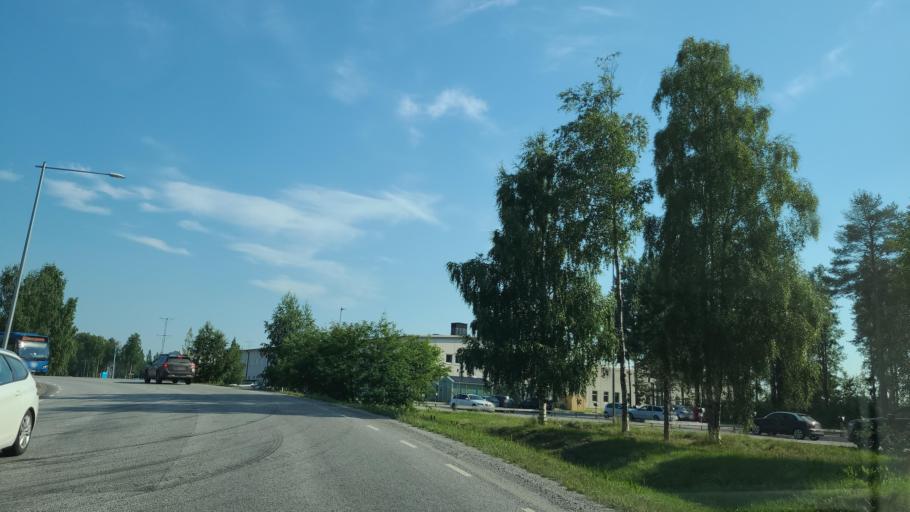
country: SE
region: Vaesterbotten
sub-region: Umea Kommun
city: Umea
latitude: 63.7982
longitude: 20.2812
